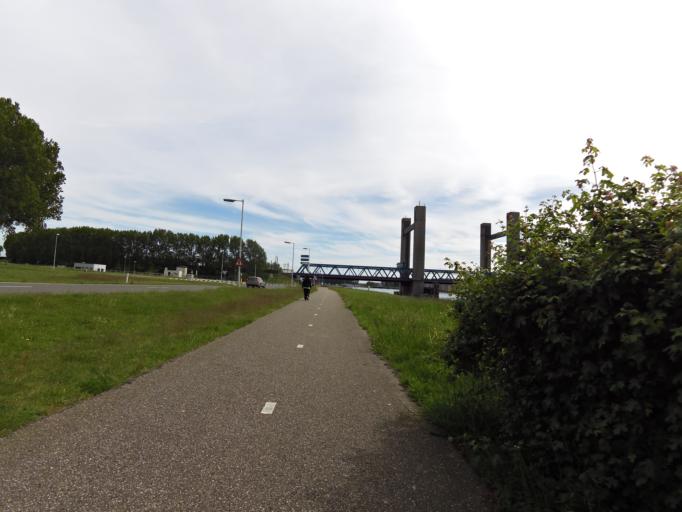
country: NL
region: South Holland
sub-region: Gemeente Maassluis
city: Maassluis
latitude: 51.9038
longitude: 4.2282
